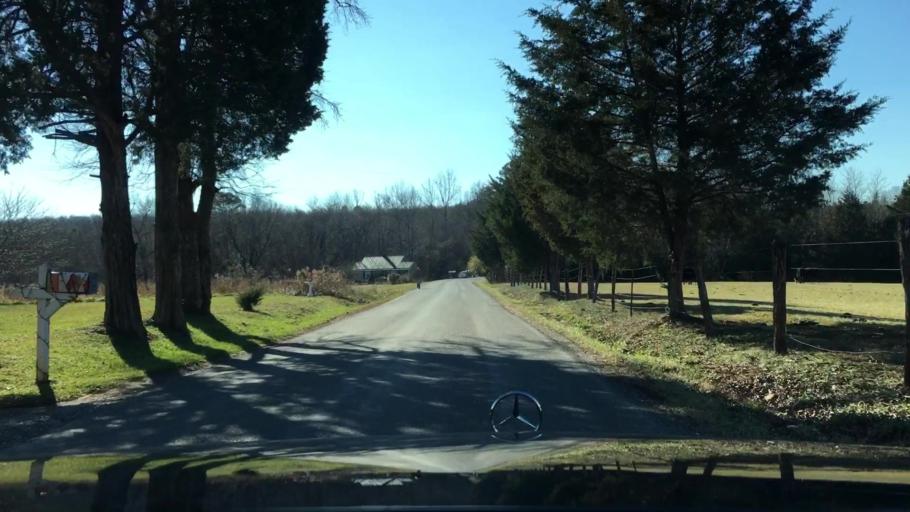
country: US
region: Virginia
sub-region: Campbell County
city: Altavista
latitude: 37.1883
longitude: -79.3153
